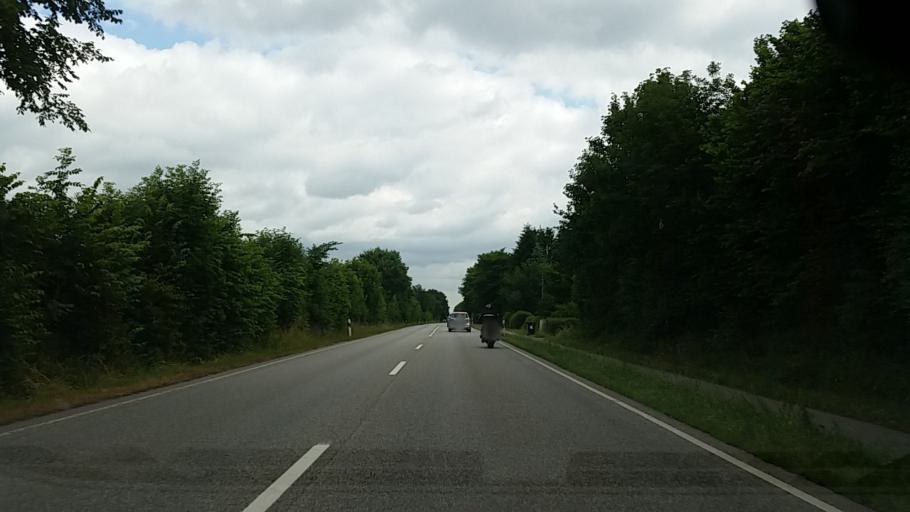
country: DE
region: Schleswig-Holstein
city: Tangstedt
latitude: 53.7222
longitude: 10.0905
